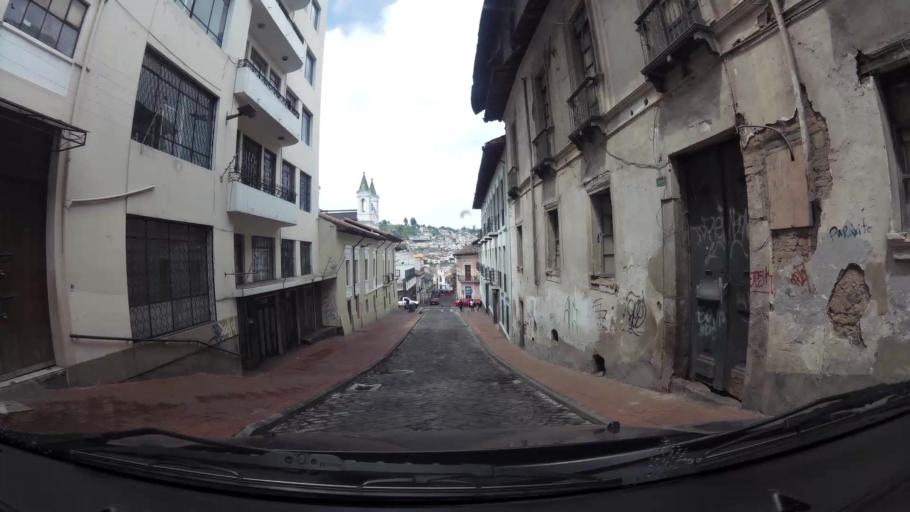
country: EC
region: Pichincha
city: Quito
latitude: -0.2172
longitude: -78.5110
